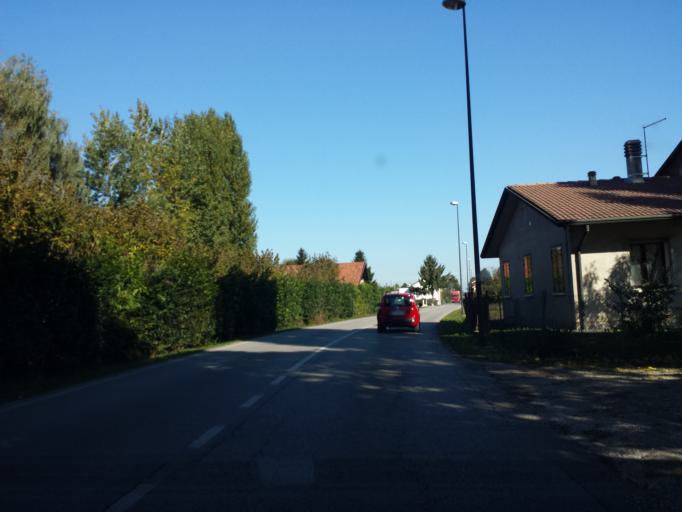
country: IT
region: Veneto
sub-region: Provincia di Vicenza
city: Camisano Vicentino
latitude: 45.5382
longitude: 11.7167
